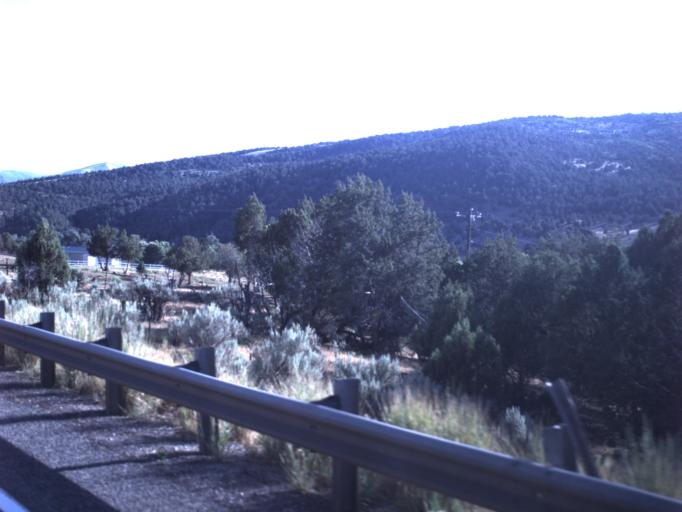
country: US
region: Utah
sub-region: Utah County
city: Woodland Hills
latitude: 39.8978
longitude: -111.5499
